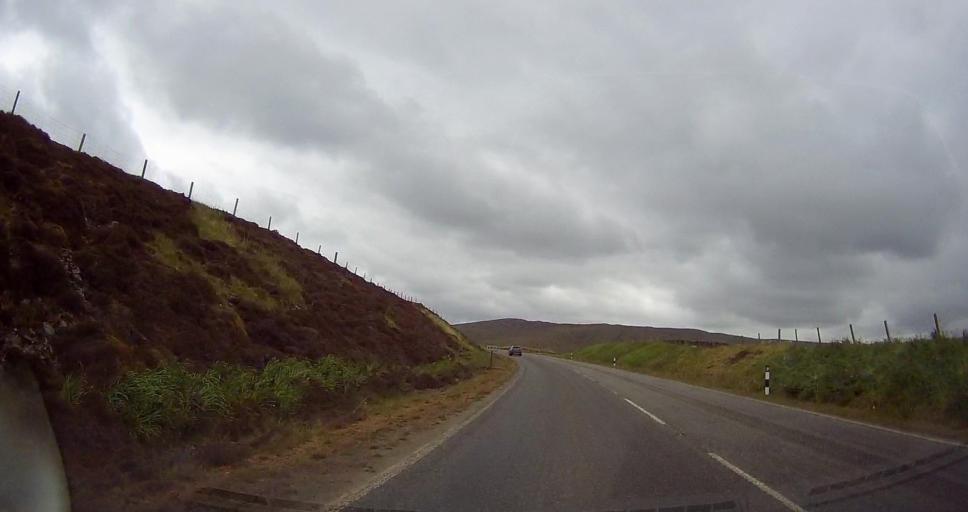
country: GB
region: Scotland
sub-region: Shetland Islands
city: Lerwick
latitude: 60.3735
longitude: -1.3365
